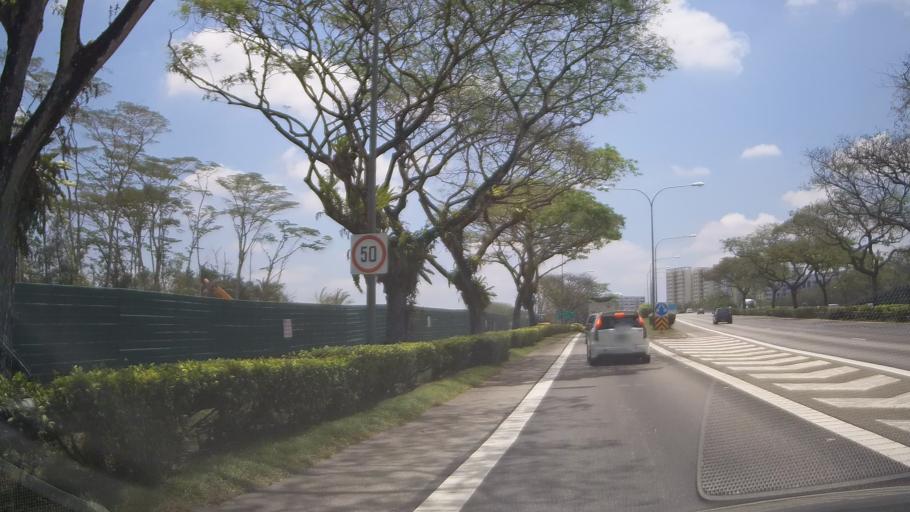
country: MY
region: Johor
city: Johor Bahru
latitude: 1.3573
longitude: 103.7149
